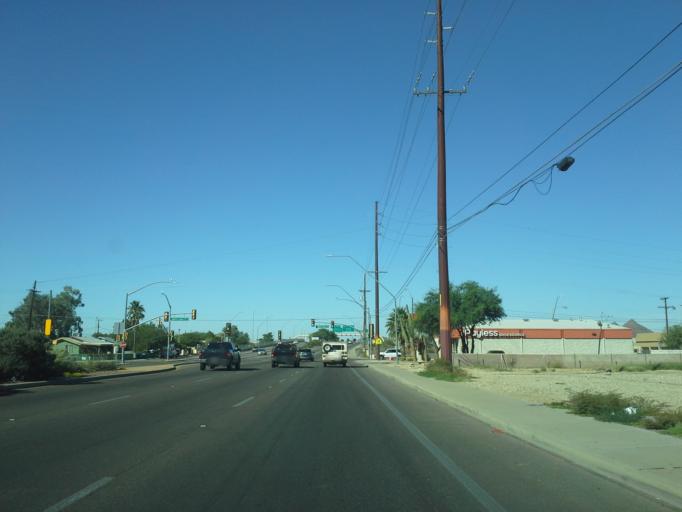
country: US
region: Arizona
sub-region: Pima County
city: Drexel Heights
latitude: 32.1341
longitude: -110.9807
